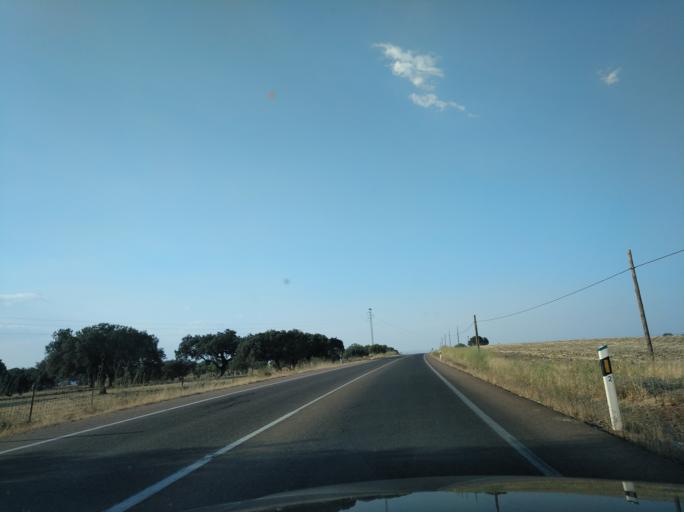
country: ES
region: Extremadura
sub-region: Provincia de Badajoz
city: Olivenza
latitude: 38.7124
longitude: -7.0855
